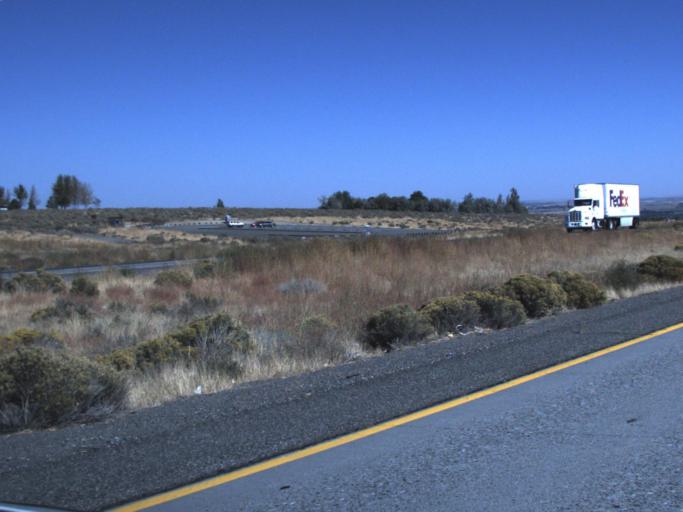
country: US
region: Washington
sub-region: Benton County
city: West Richland
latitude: 46.2452
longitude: -119.3498
